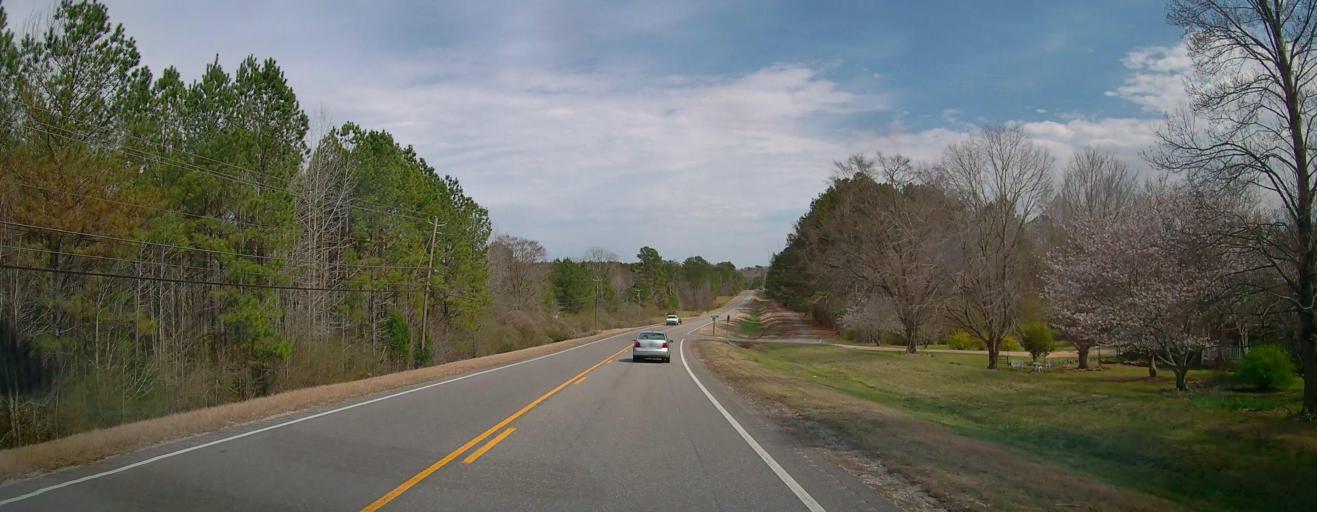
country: US
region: Alabama
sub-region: Walker County
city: Carbon Hill
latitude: 33.9232
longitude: -87.5885
